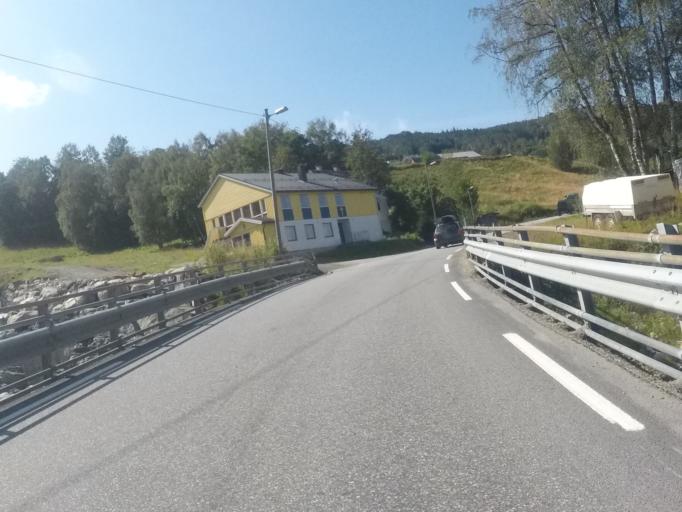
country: NO
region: Sogn og Fjordane
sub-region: Hornindal
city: Hornindal
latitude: 61.8037
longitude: 6.5275
